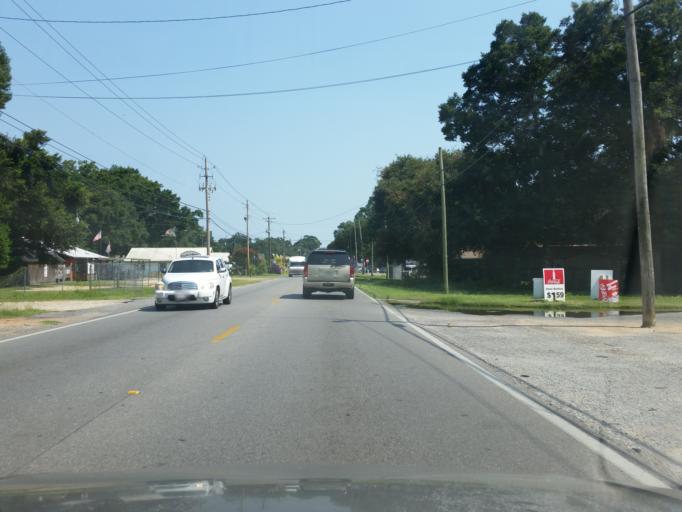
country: US
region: Florida
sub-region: Escambia County
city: Brent
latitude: 30.4925
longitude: -87.2527
